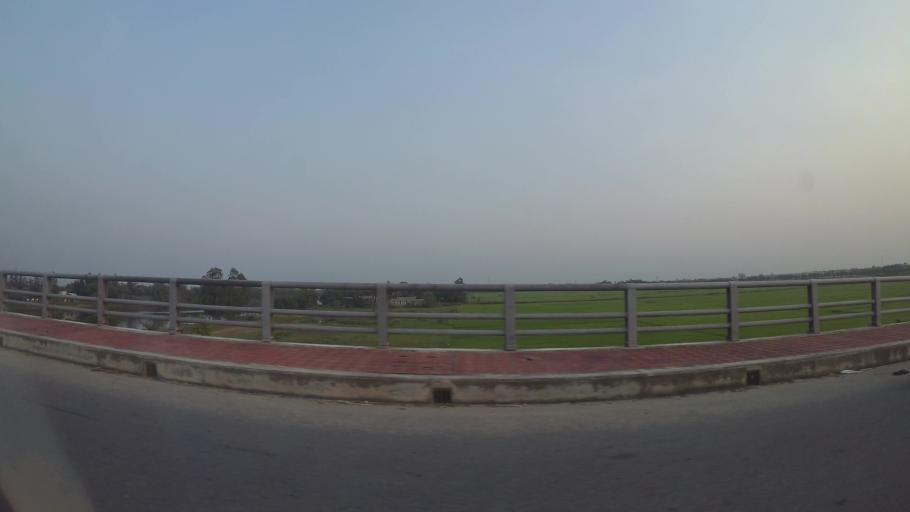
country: VN
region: Da Nang
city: Cam Le
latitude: 15.9685
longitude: 108.2167
